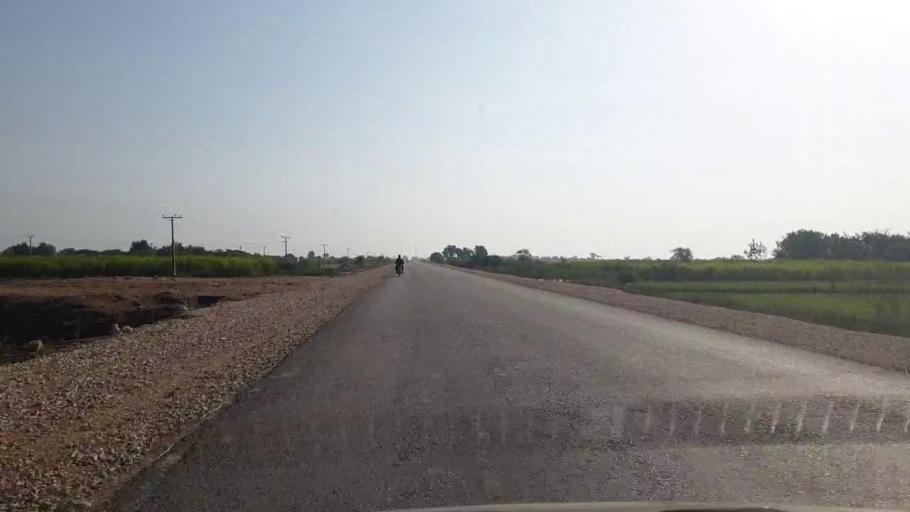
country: PK
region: Sindh
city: Badin
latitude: 24.6590
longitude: 68.9283
